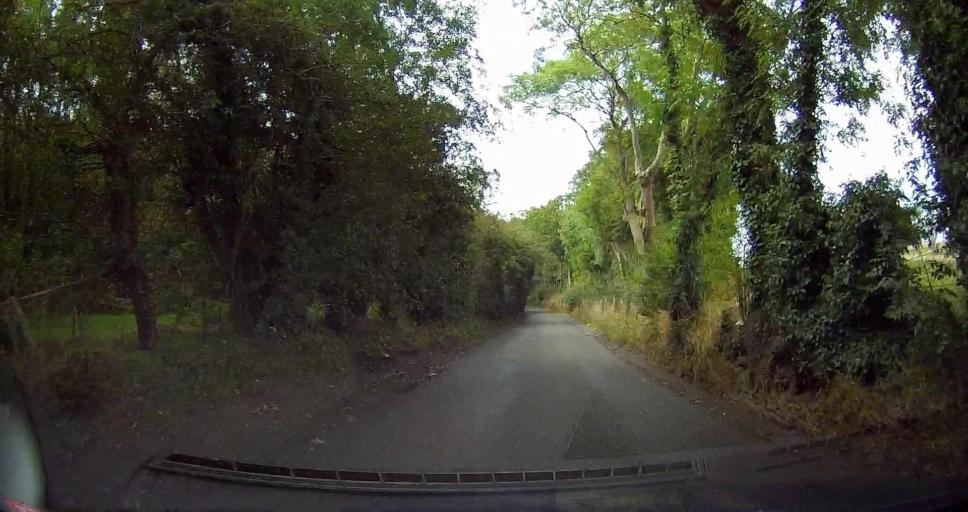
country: GB
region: England
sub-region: Kent
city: Longfield
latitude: 51.4178
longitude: 0.2961
